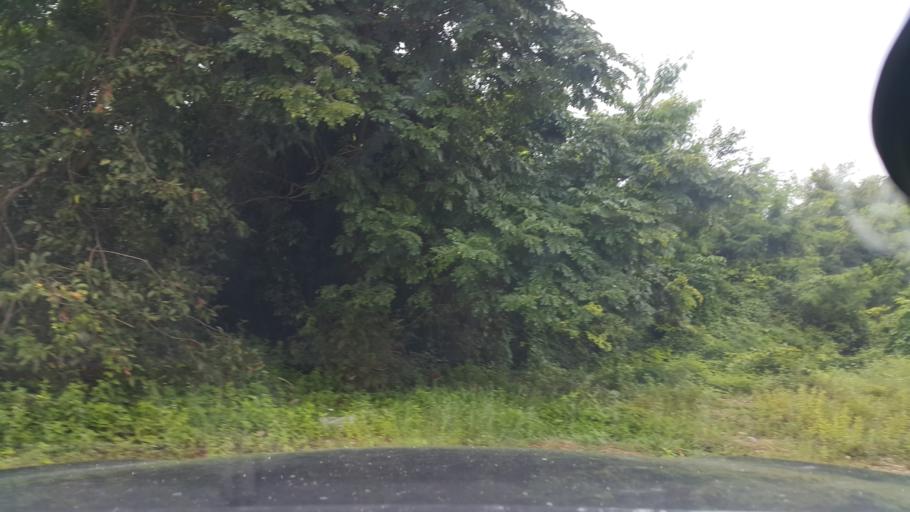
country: TH
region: Chiang Mai
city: Mae On
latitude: 18.8324
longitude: 99.1883
